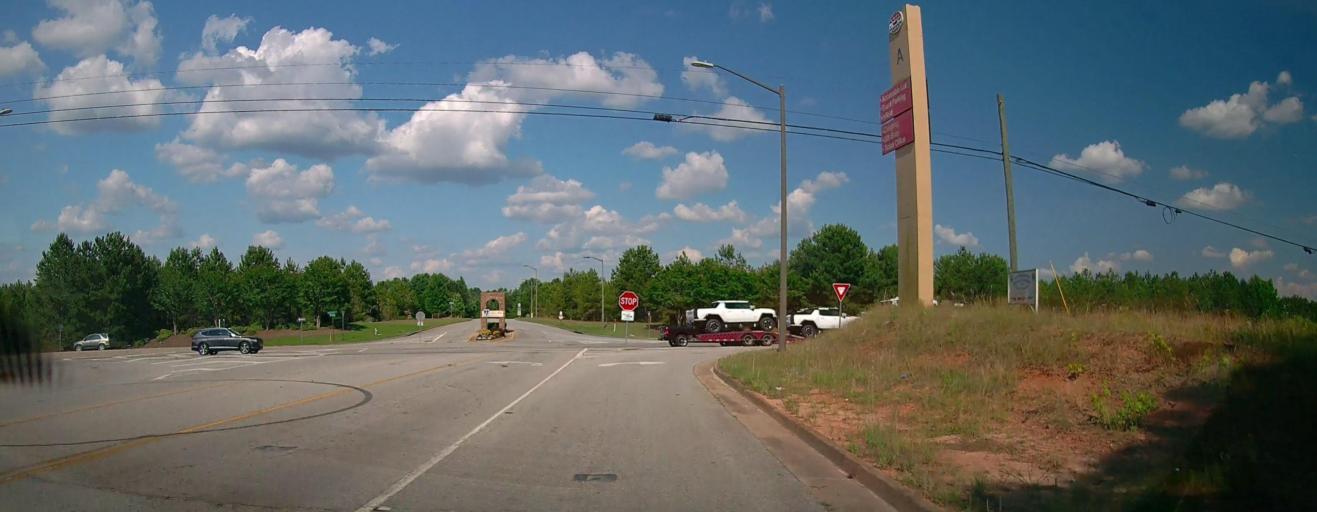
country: US
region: Georgia
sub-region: Henry County
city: Hampton
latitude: 33.3951
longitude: -84.3121
